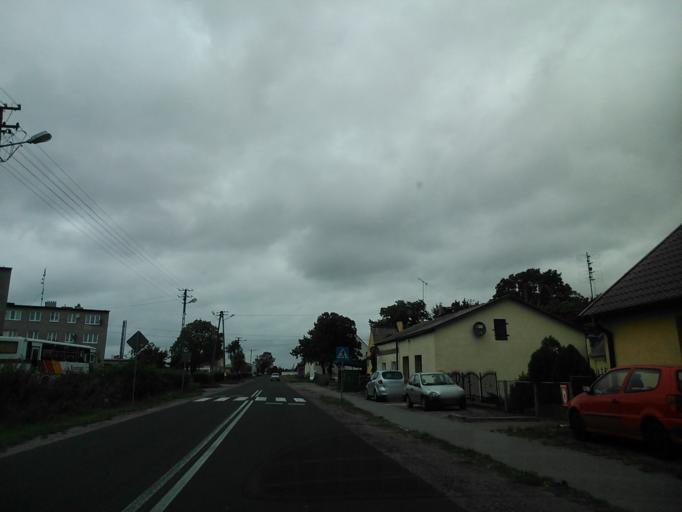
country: PL
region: Kujawsko-Pomorskie
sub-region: Powiat radziejowski
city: Piotrkow Kujawski
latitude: 52.5596
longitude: 18.4241
